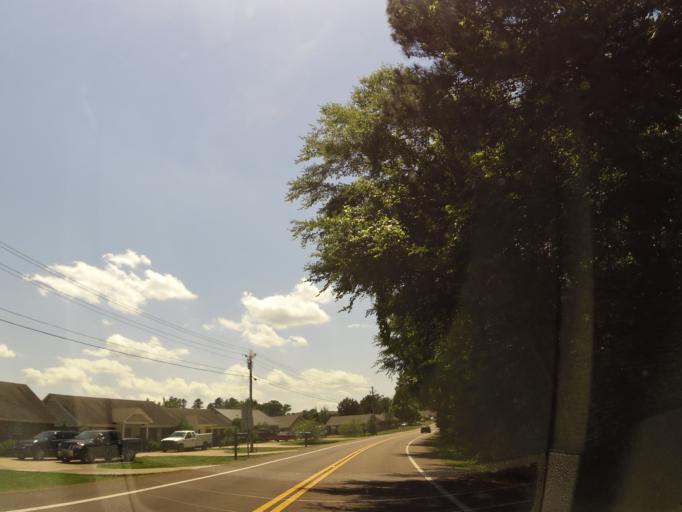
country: US
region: Mississippi
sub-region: Lafayette County
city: University
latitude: 34.3503
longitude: -89.5361
